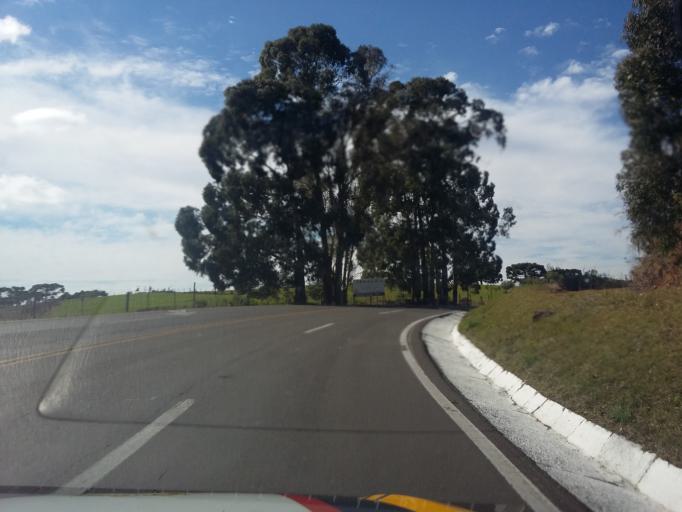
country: BR
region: Rio Grande do Sul
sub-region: Vacaria
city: Vacaria
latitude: -28.5782
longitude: -51.0231
